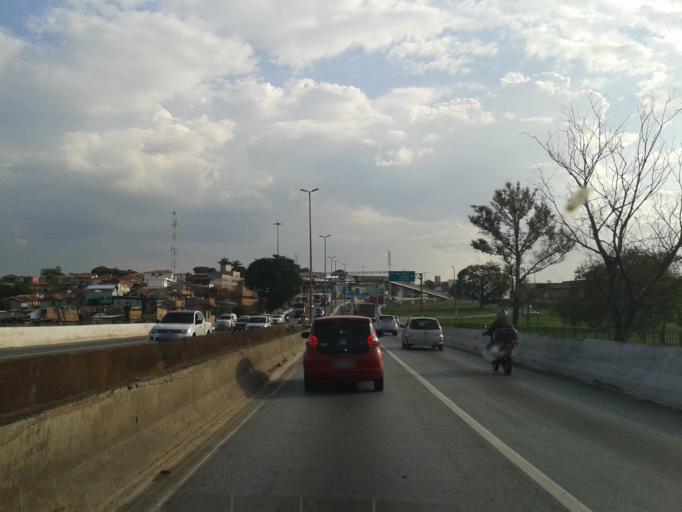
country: BR
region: Minas Gerais
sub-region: Belo Horizonte
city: Belo Horizonte
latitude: -19.8784
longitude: -43.9523
